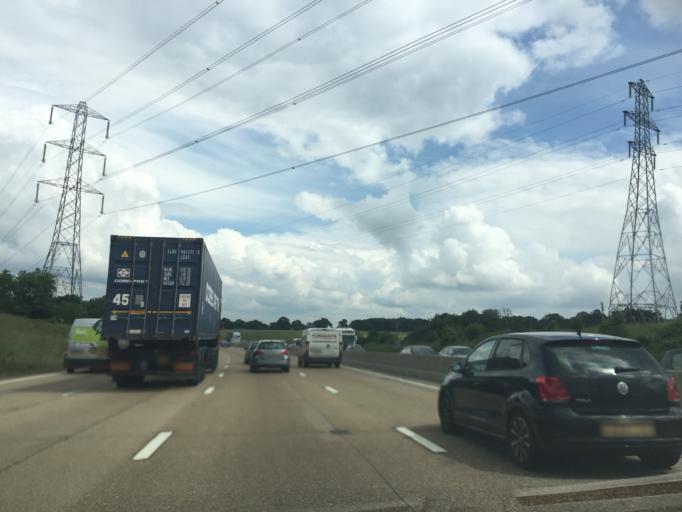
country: GB
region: England
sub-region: Greater London
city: Hadley Wood
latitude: 51.6854
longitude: -0.1514
